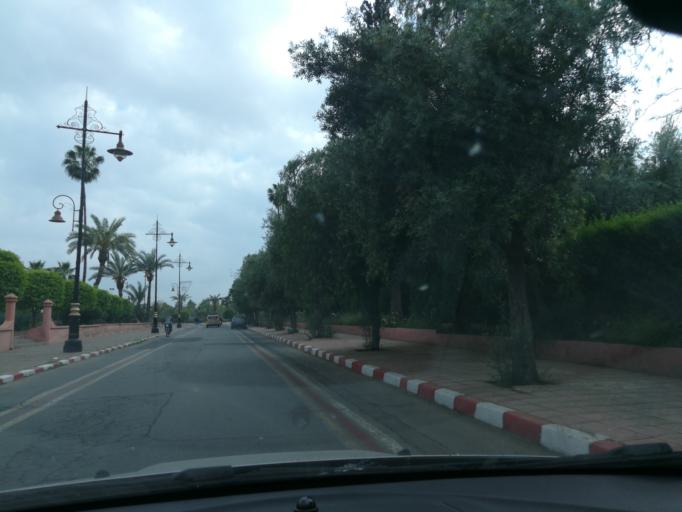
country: MA
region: Marrakech-Tensift-Al Haouz
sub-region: Marrakech
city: Marrakesh
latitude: 31.6196
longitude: -8.0060
